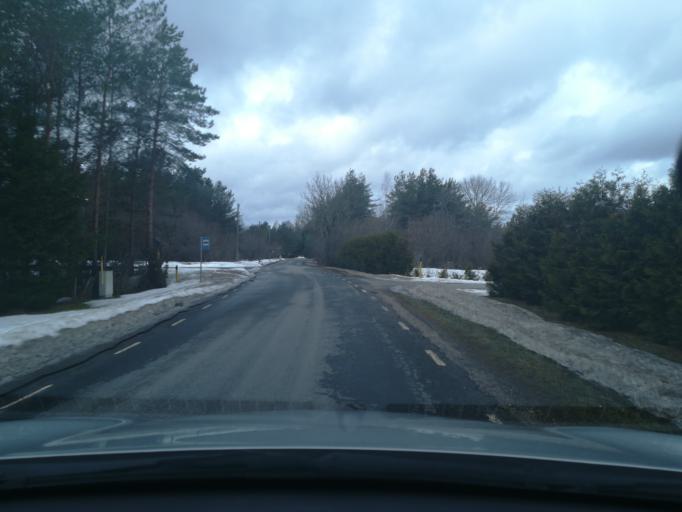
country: EE
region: Harju
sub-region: Saue linn
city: Saue
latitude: 59.3641
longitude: 24.5152
